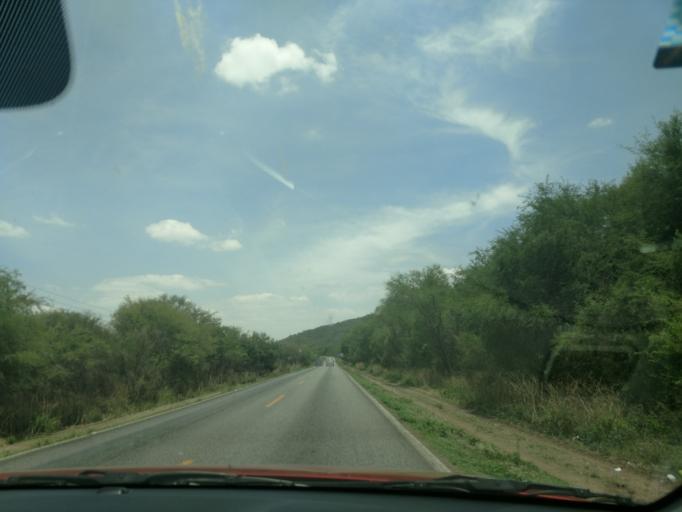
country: MX
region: San Luis Potosi
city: Ciudad Fernandez
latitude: 21.9976
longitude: -100.1397
